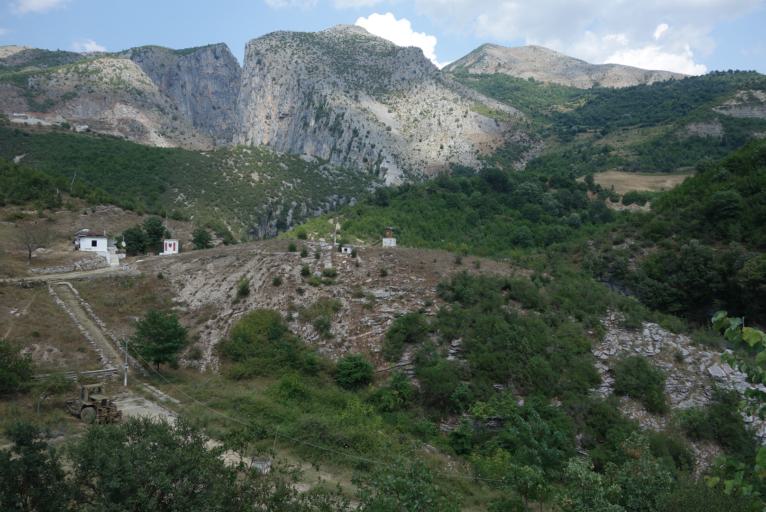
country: AL
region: Berat
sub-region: Rrethi i Skraparit
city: Corovode
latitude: 40.5176
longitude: 20.2459
